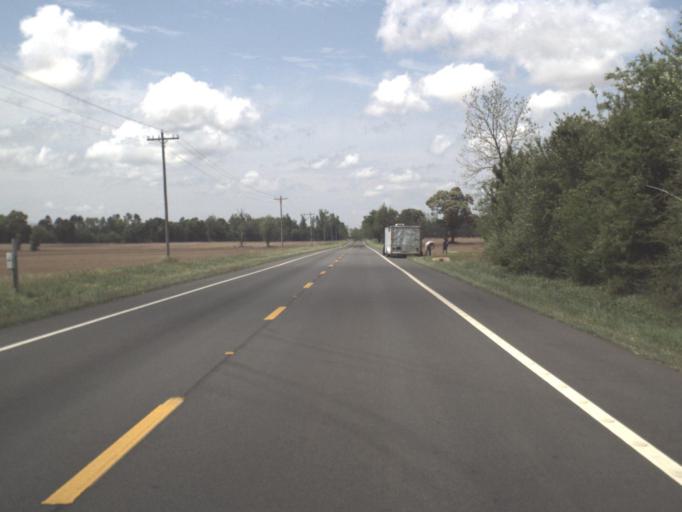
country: US
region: Florida
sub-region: Escambia County
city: Century
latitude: 30.8518
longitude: -87.1496
